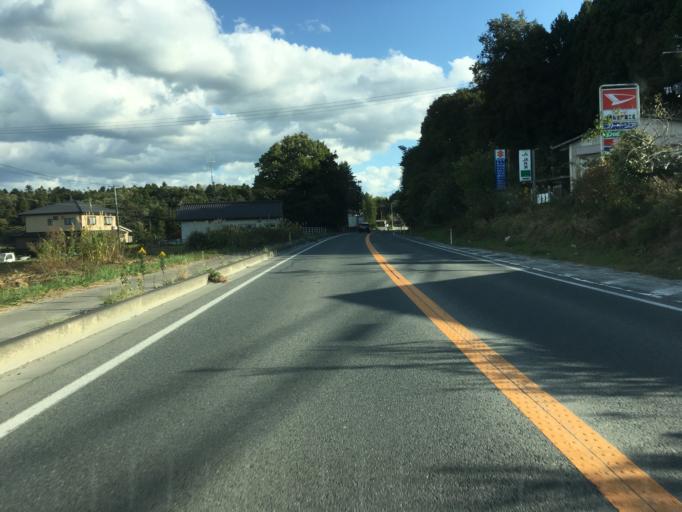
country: JP
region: Miyagi
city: Marumori
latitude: 37.8884
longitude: 140.9123
